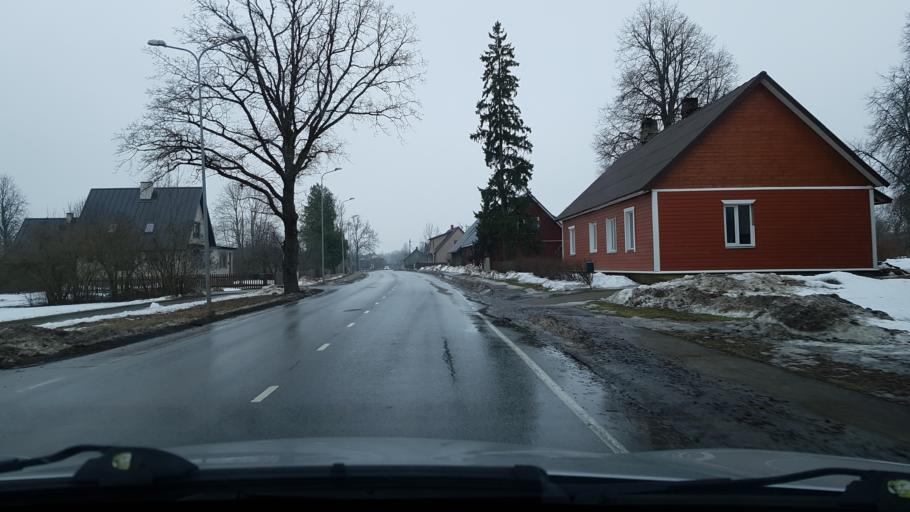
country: EE
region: Valgamaa
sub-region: Torva linn
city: Torva
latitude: 58.2406
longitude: 25.8573
